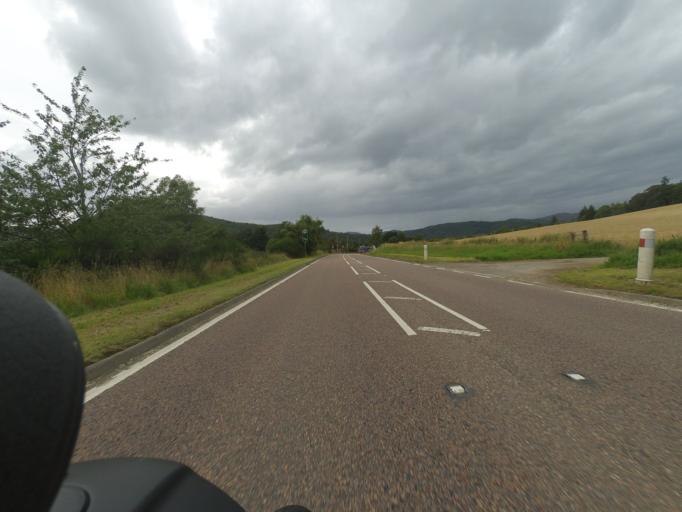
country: GB
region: Scotland
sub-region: Highland
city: Muir of Ord
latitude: 57.5628
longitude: -4.5727
